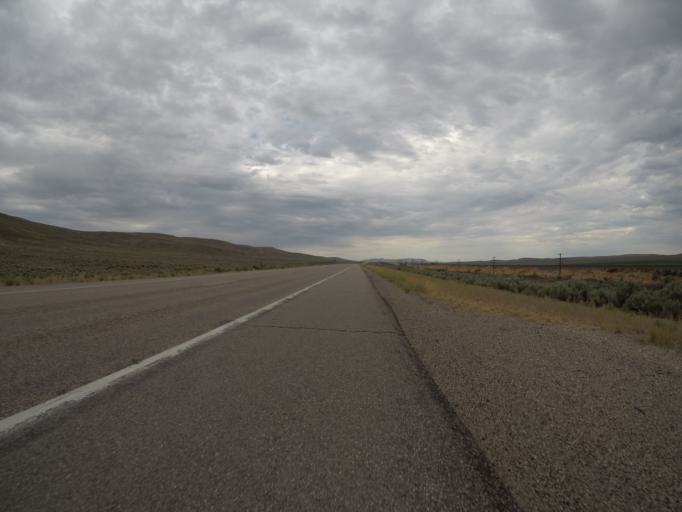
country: US
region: Utah
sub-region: Rich County
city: Randolph
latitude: 41.8452
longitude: -110.9746
